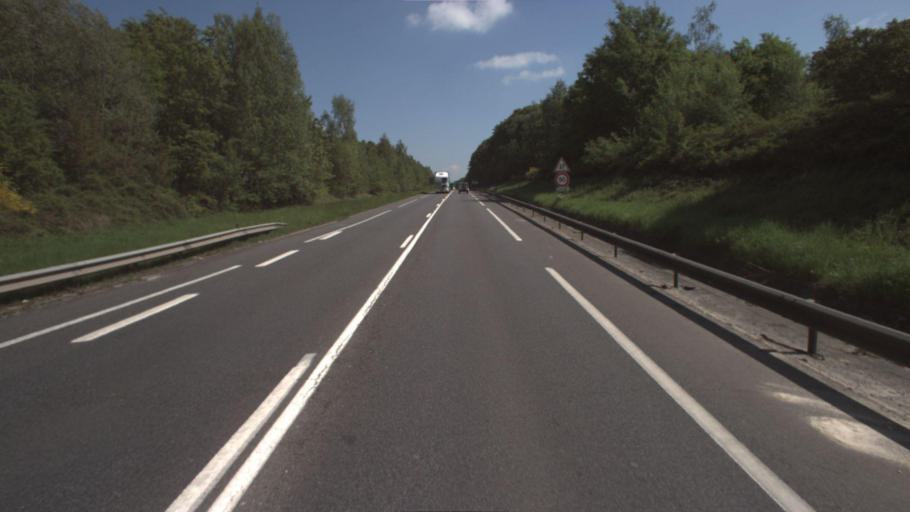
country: FR
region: Ile-de-France
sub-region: Departement de Seine-et-Marne
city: Guignes
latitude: 48.6426
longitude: 2.7960
